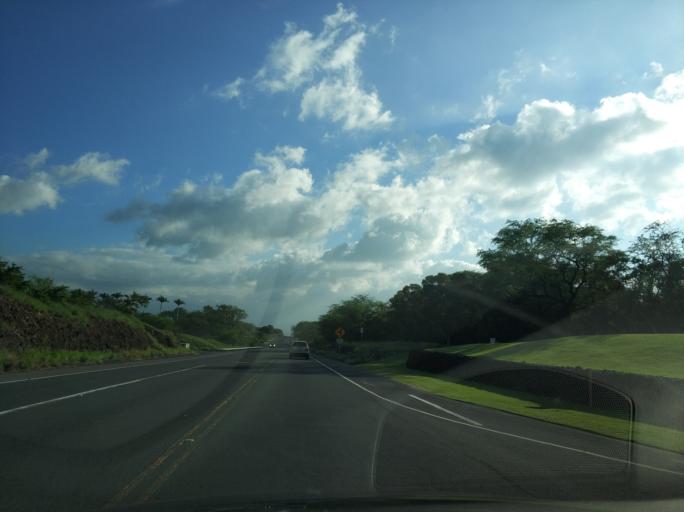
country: US
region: Hawaii
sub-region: Hawaii County
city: Waikoloa
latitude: 20.0061
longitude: -155.8143
